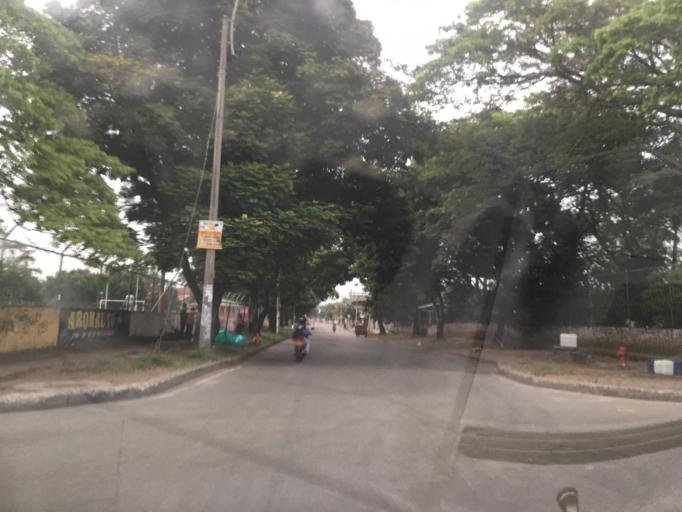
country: CO
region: Valle del Cauca
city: Cali
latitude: 3.4190
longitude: -76.5220
